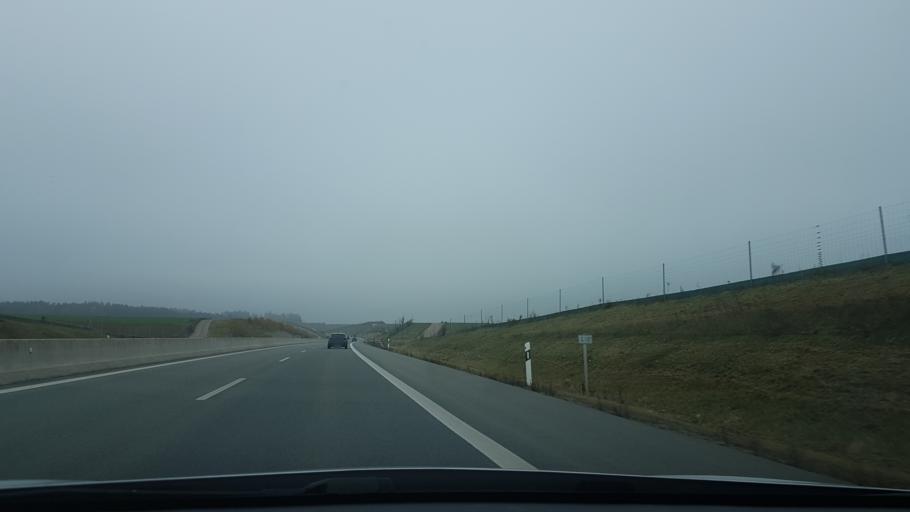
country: DE
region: Bavaria
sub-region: Lower Bavaria
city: Ergoldsbach
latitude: 48.6965
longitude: 12.1794
